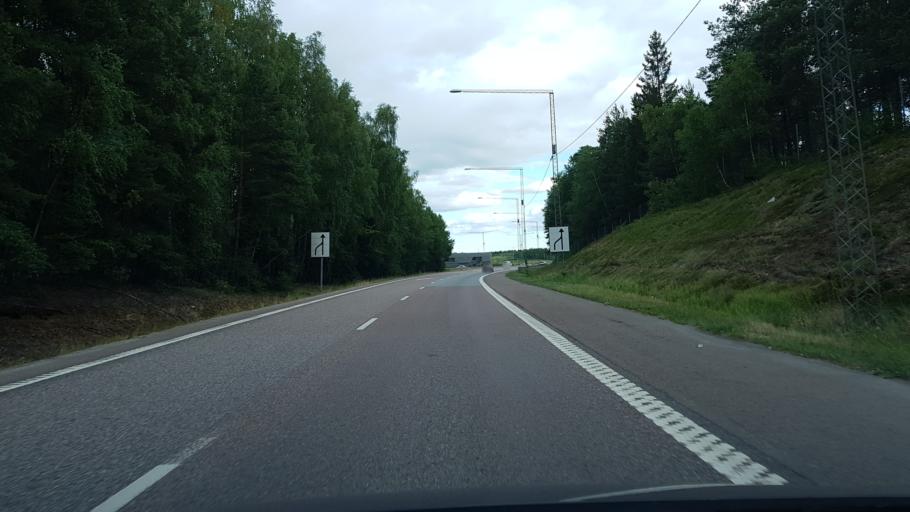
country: SE
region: Stockholm
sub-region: Sigtuna Kommun
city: Rosersberg
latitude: 59.6131
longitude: 17.8975
